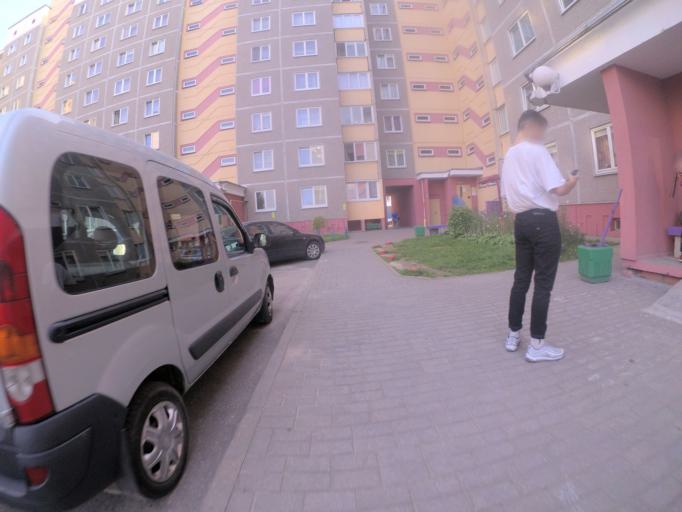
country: BY
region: Grodnenskaya
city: Hrodna
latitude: 53.6975
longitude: 23.8347
